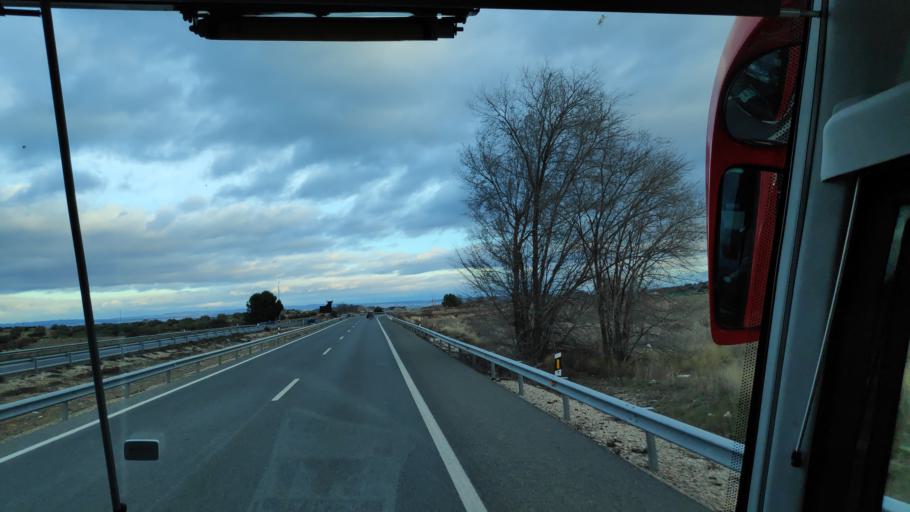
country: ES
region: Madrid
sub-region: Provincia de Madrid
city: Villarejo de Salvanes
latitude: 40.1513
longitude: -3.2381
